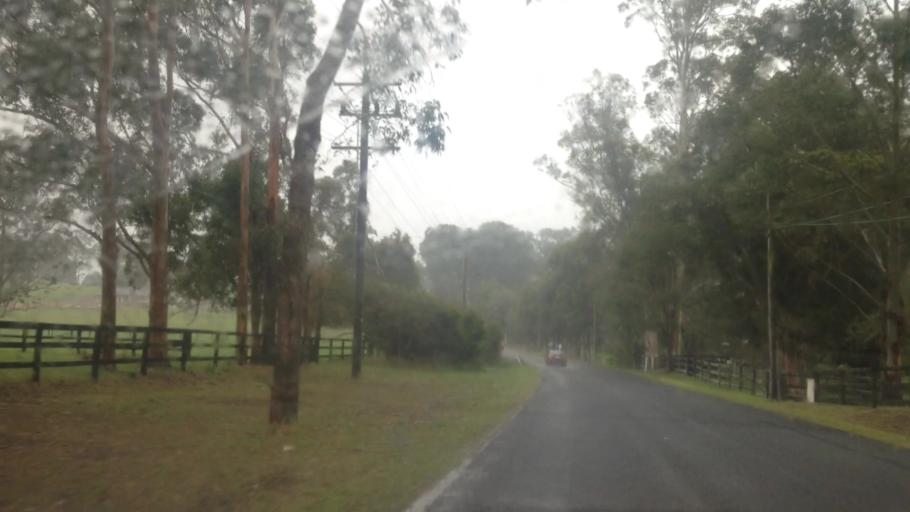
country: AU
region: New South Wales
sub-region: Wyong Shire
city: Little Jilliby
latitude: -33.2048
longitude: 151.3637
